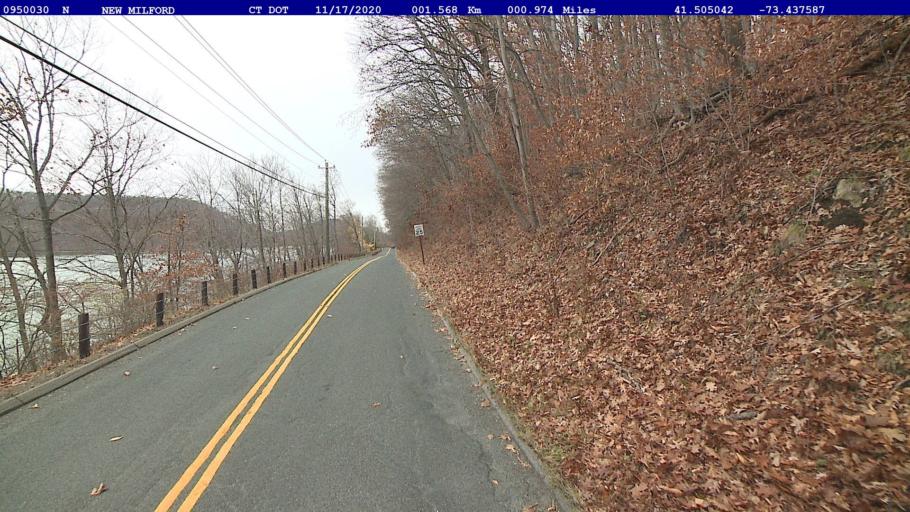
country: US
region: Connecticut
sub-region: Litchfield County
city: New Milford
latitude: 41.5050
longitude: -73.4376
